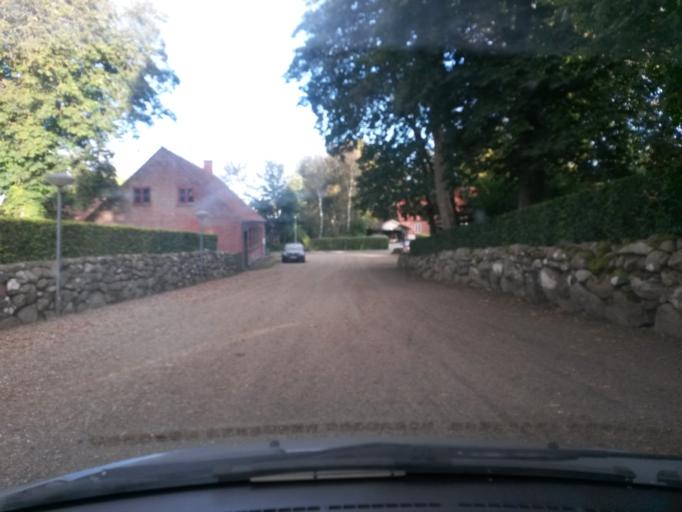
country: DK
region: Central Jutland
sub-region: Silkeborg Kommune
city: Kjellerup
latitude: 56.3285
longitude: 9.3746
